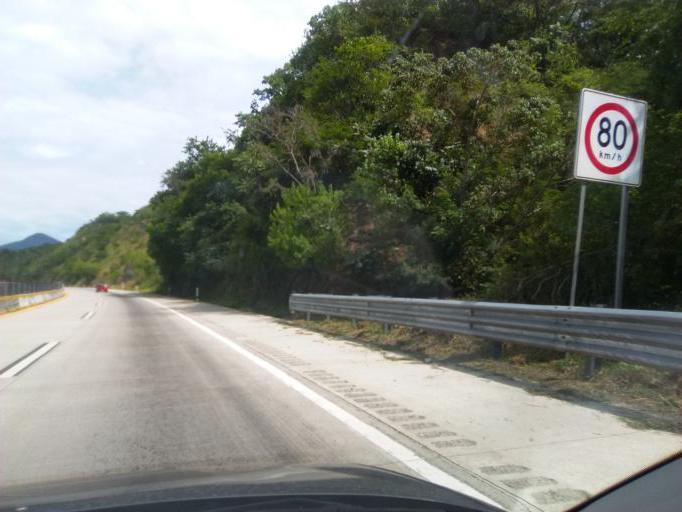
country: MX
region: Guerrero
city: Tierra Colorada
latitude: 17.1876
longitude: -99.5431
